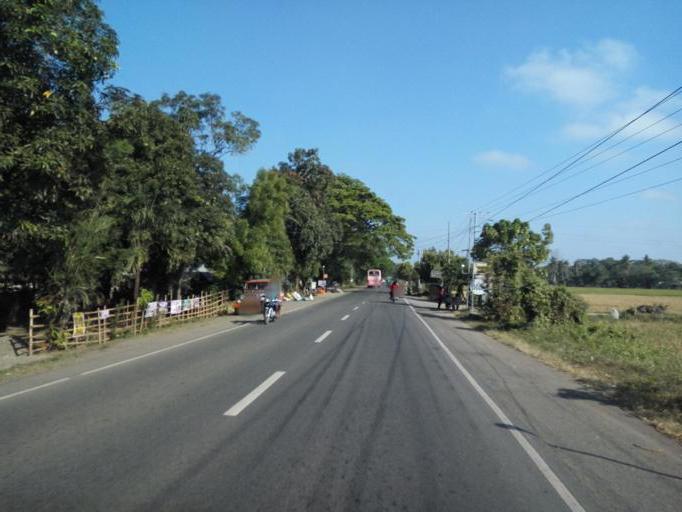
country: PH
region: Cagayan Valley
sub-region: Province of Cagayan
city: Amulung
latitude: 17.8572
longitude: 121.7186
